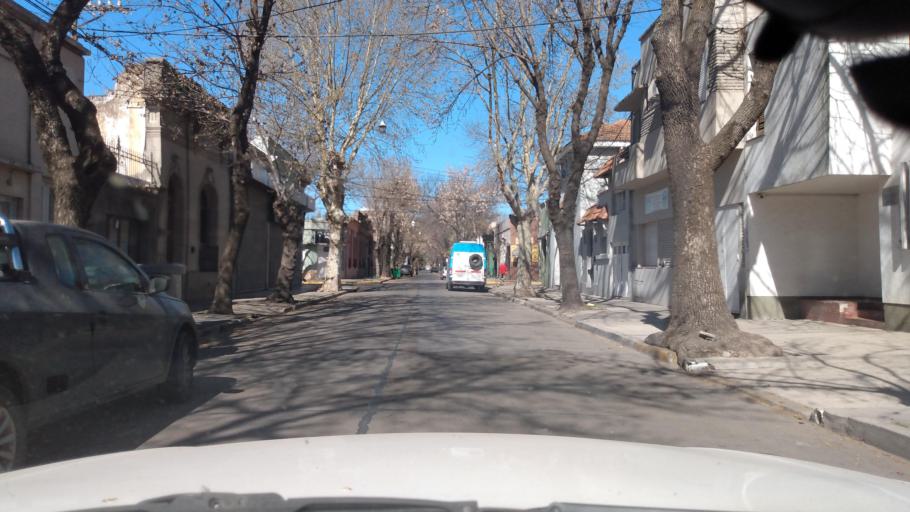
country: AR
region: Buenos Aires
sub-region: Partido de Mercedes
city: Mercedes
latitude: -34.6496
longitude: -59.4288
